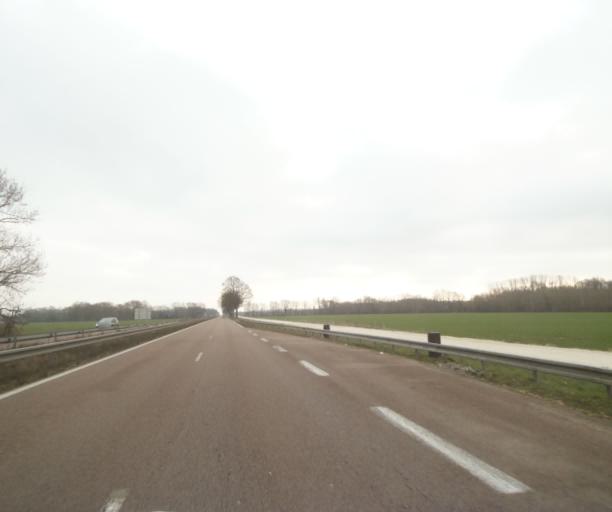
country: FR
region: Champagne-Ardenne
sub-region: Departement de la Marne
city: Pargny-sur-Saulx
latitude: 48.6792
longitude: 4.7528
